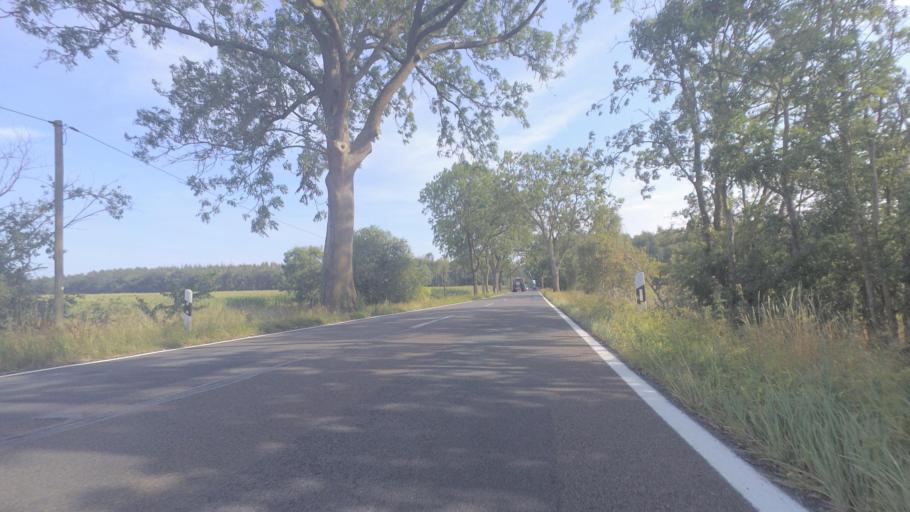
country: DE
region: Mecklenburg-Vorpommern
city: Grimmen
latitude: 54.0446
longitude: 13.1218
